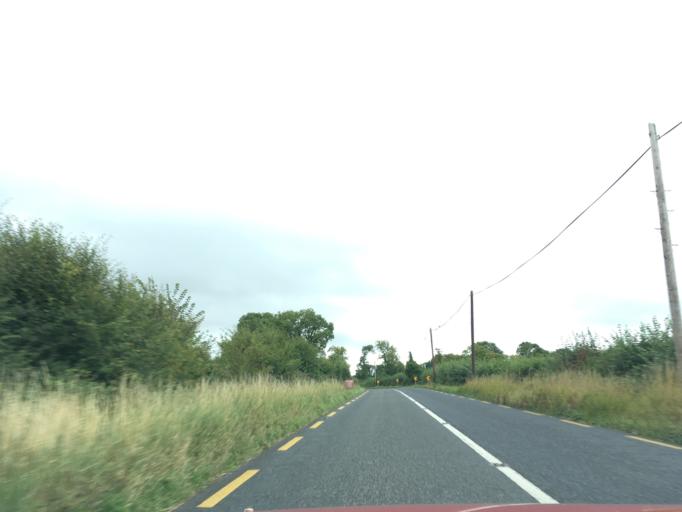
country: IE
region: Munster
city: Fethard
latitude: 52.4395
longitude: -7.7972
